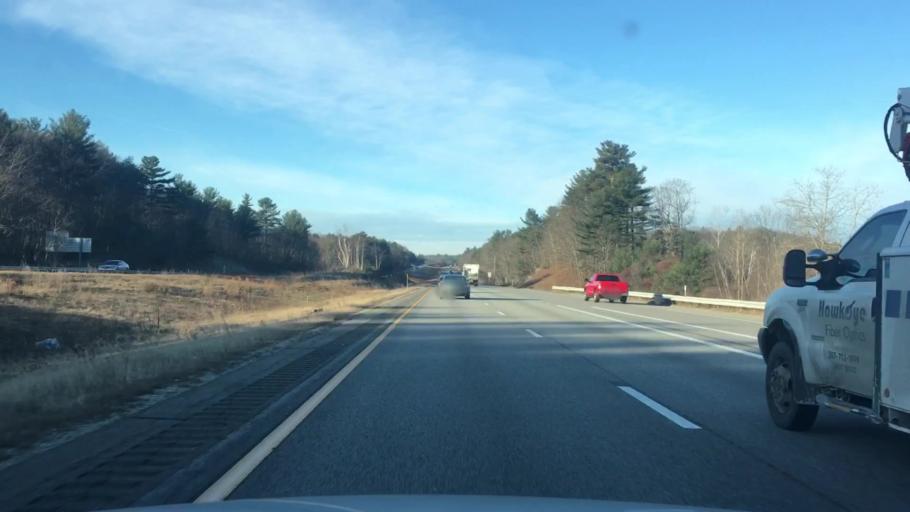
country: US
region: New Hampshire
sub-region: Rockingham County
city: Raymond
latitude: 43.0237
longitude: -71.2007
